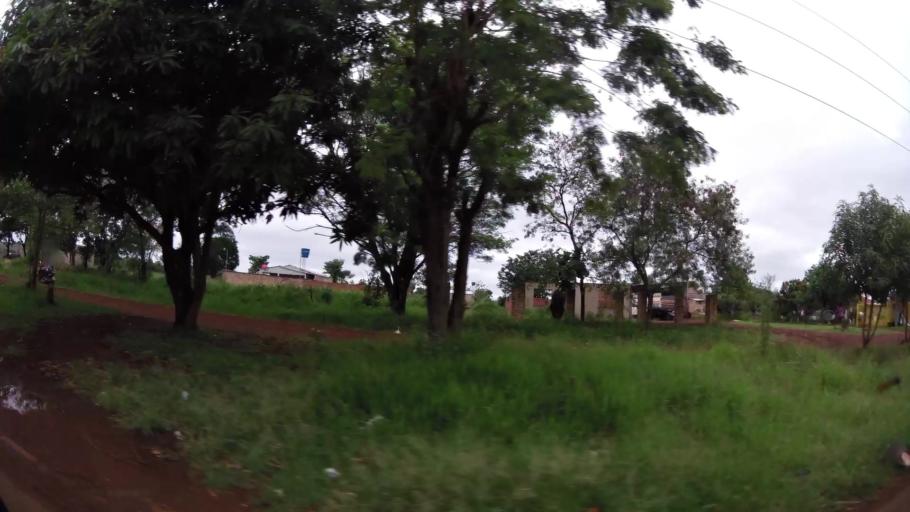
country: PY
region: Alto Parana
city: Presidente Franco
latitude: -25.5150
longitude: -54.6783
